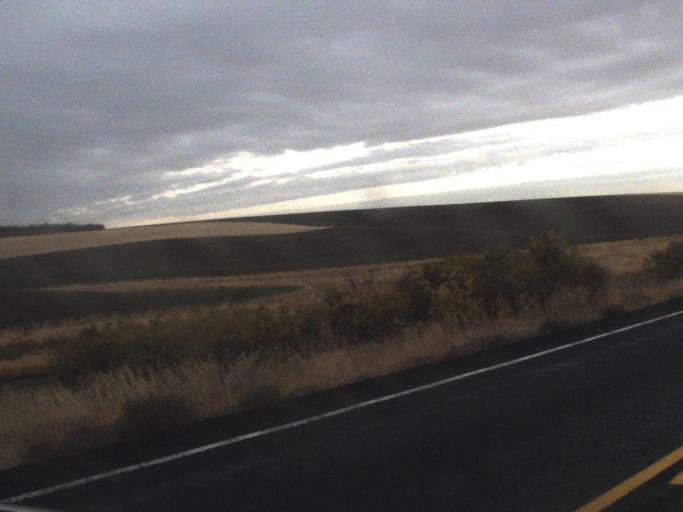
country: US
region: Washington
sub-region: Lincoln County
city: Davenport
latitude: 47.7201
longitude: -118.1516
